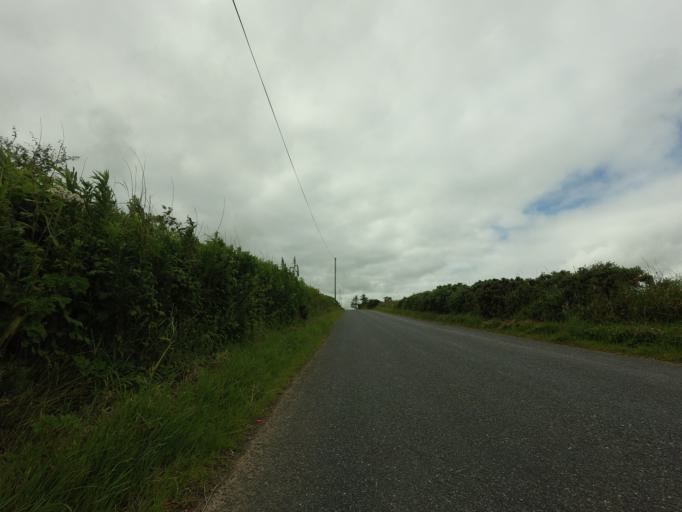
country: GB
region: Scotland
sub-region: Aberdeenshire
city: Rosehearty
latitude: 57.5412
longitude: -2.2037
